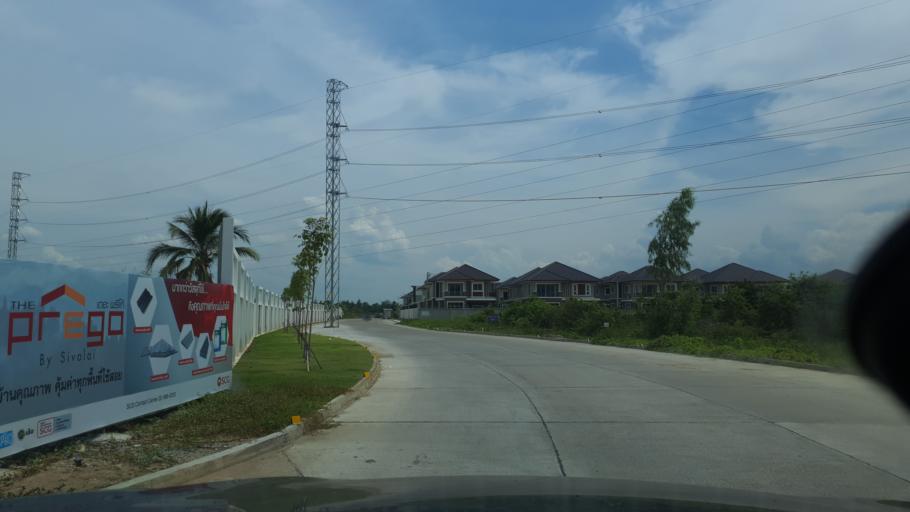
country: TH
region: Chiang Mai
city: Saraphi
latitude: 18.7399
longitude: 99.0736
